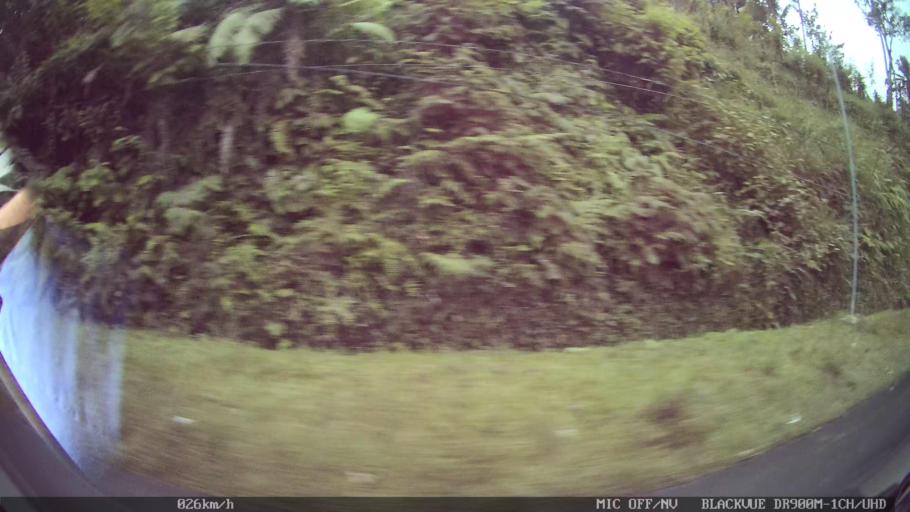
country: ID
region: Bali
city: Peneng
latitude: -8.3620
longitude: 115.2169
